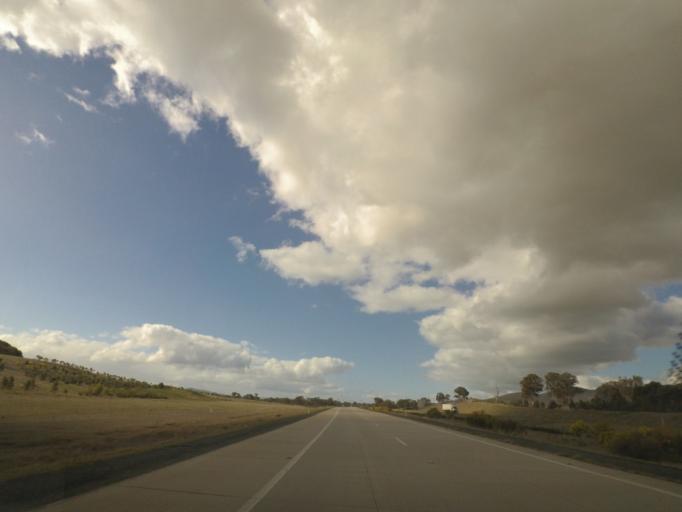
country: AU
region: New South Wales
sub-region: Greater Hume Shire
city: Holbrook
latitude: -35.7002
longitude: 147.3344
